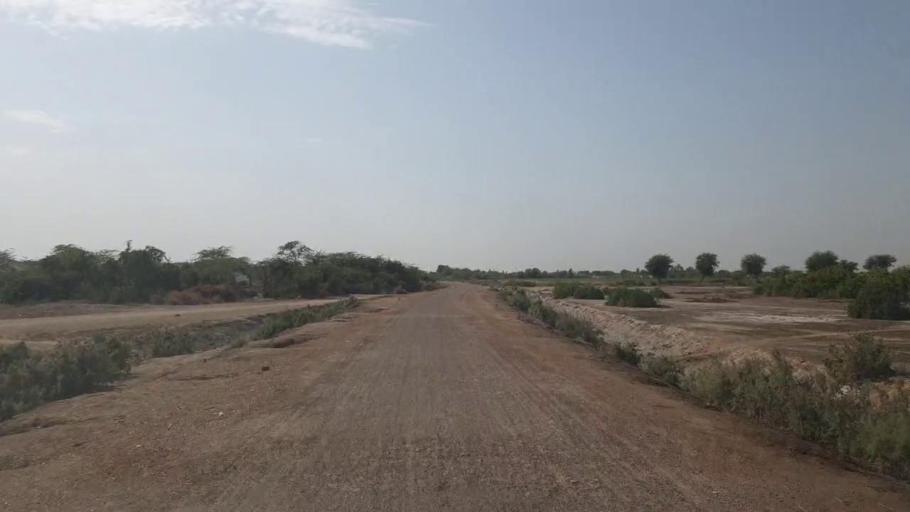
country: PK
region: Sindh
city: Dhoro Naro
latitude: 25.4238
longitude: 69.5746
